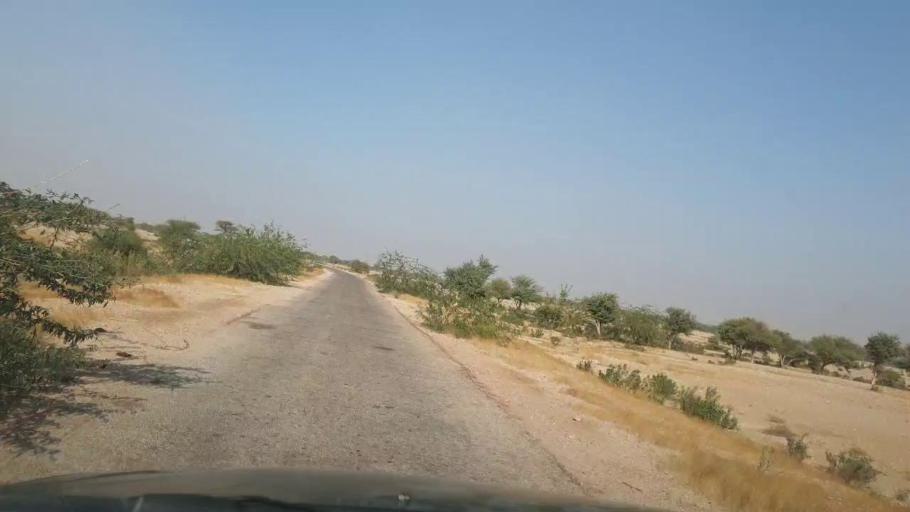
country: PK
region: Sindh
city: Jamshoro
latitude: 25.5521
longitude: 67.8287
